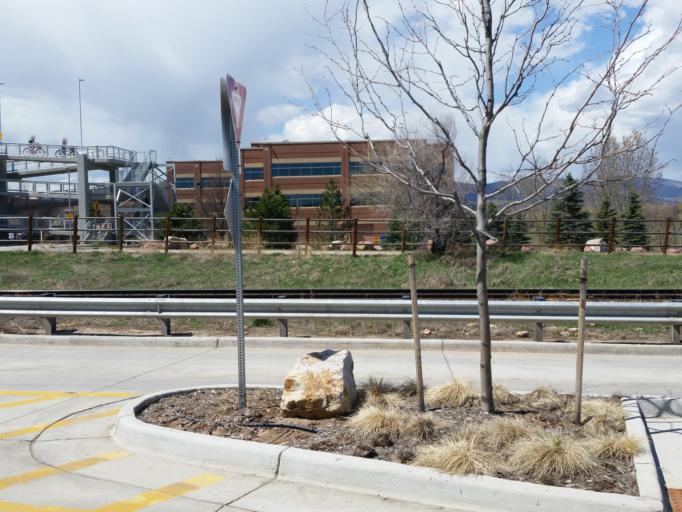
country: US
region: Colorado
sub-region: Larimer County
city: Fort Collins
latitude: 40.5604
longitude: -105.0794
